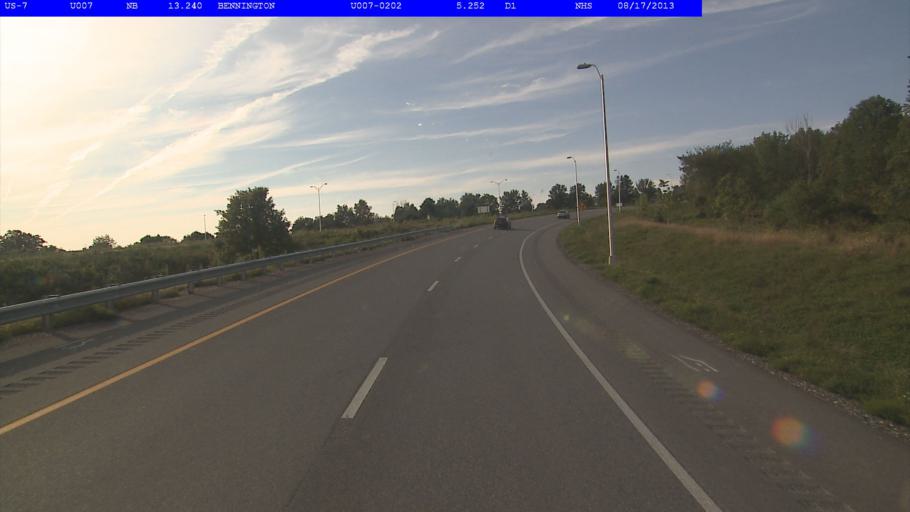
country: US
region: Vermont
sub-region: Bennington County
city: Bennington
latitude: 42.9069
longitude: -73.2072
